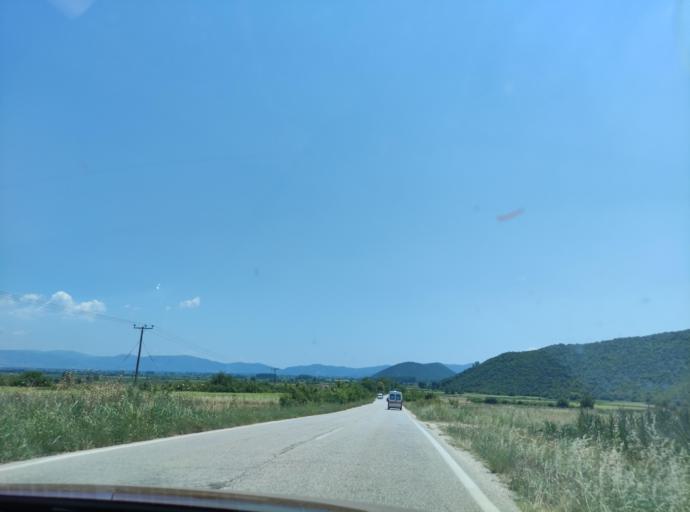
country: GR
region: East Macedonia and Thrace
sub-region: Nomos Kavalas
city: Palaiochori
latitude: 40.9710
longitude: 24.1665
